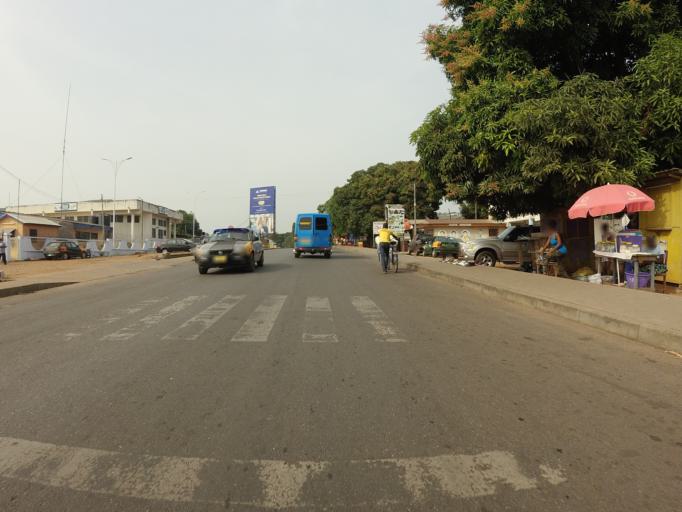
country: GH
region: Volta
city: Ho
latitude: 6.6122
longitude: 0.4625
